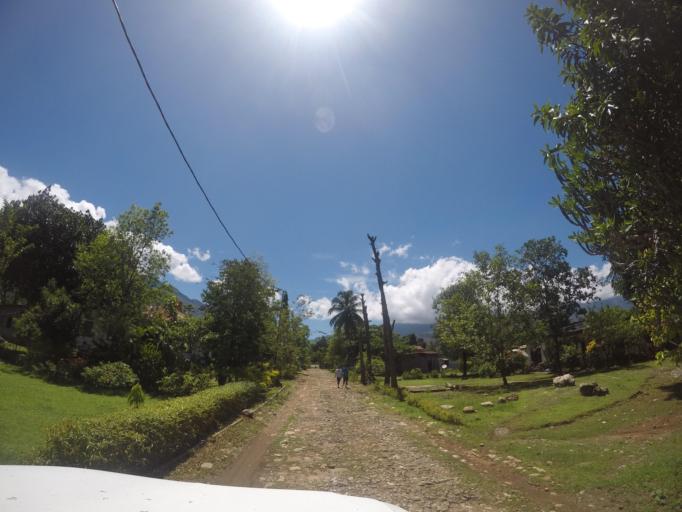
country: TL
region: Bobonaro
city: Maliana
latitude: -8.9804
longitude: 125.2191
